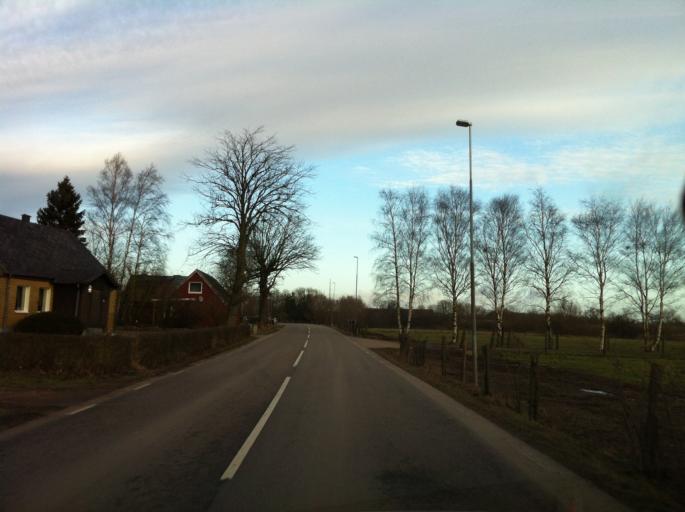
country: SE
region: Skane
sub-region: Landskrona
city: Asmundtorp
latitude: 55.8849
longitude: 12.9701
